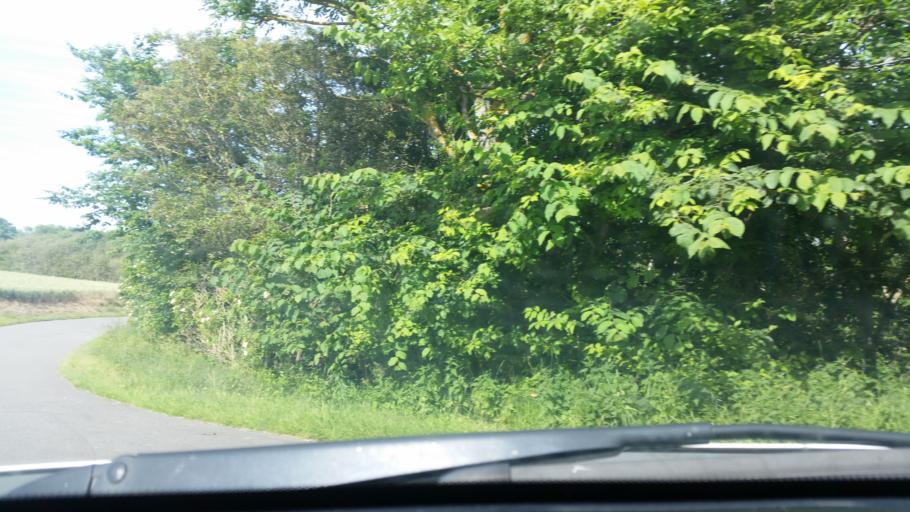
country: DK
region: Central Jutland
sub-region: Samso Kommune
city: Tranebjerg
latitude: 55.7706
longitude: 10.5518
